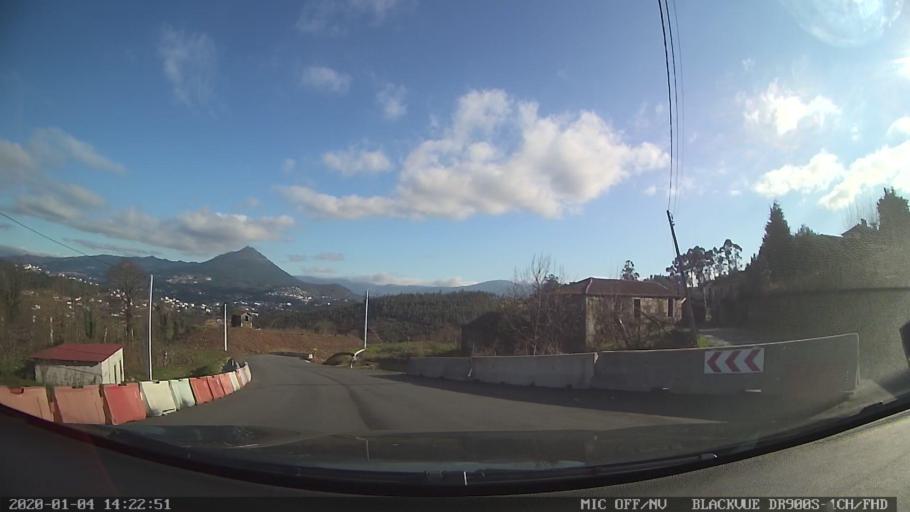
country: PT
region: Braga
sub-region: Celorico de Basto
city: Celorico de Basto
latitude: 41.4079
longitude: -7.9847
